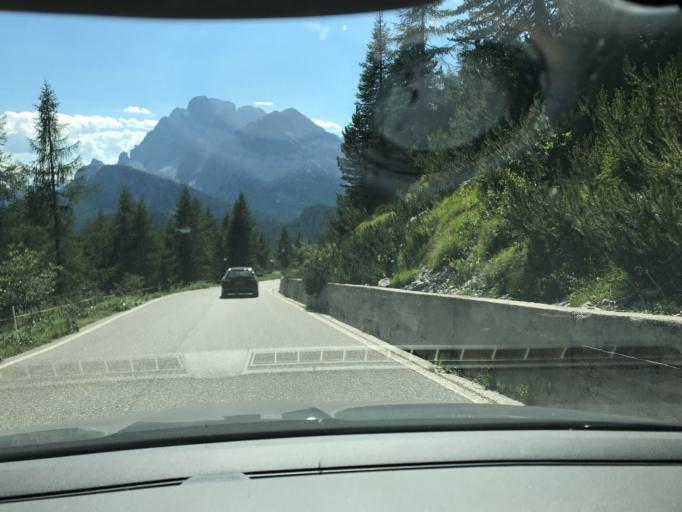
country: IT
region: Trentino-Alto Adige
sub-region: Bolzano
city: Sesto
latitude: 46.6083
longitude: 12.2850
